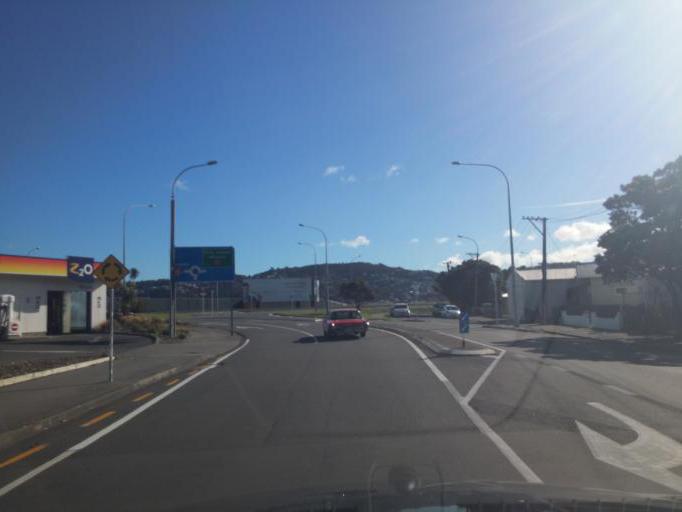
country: NZ
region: Wellington
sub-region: Wellington City
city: Wellington
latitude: -41.3254
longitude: 174.8106
